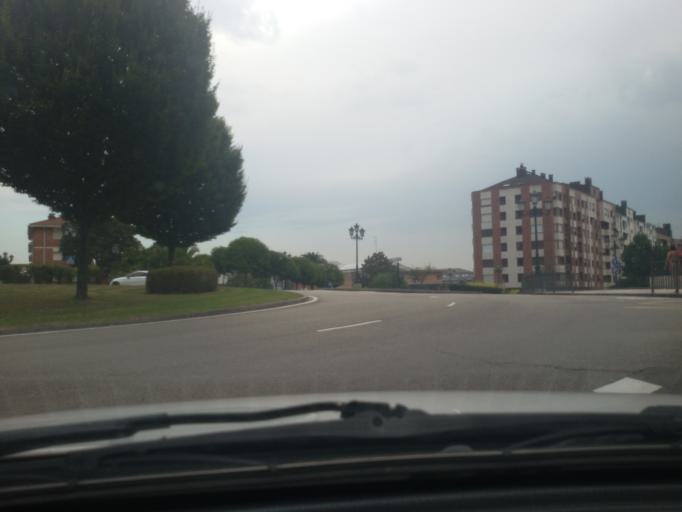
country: ES
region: Asturias
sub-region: Province of Asturias
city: Oviedo
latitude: 43.3696
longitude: -5.8484
